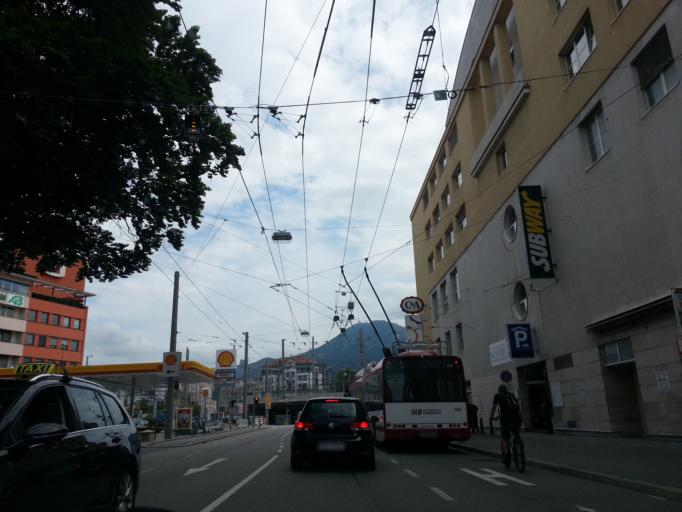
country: AT
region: Salzburg
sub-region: Salzburg Stadt
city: Salzburg
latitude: 47.8108
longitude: 13.0419
